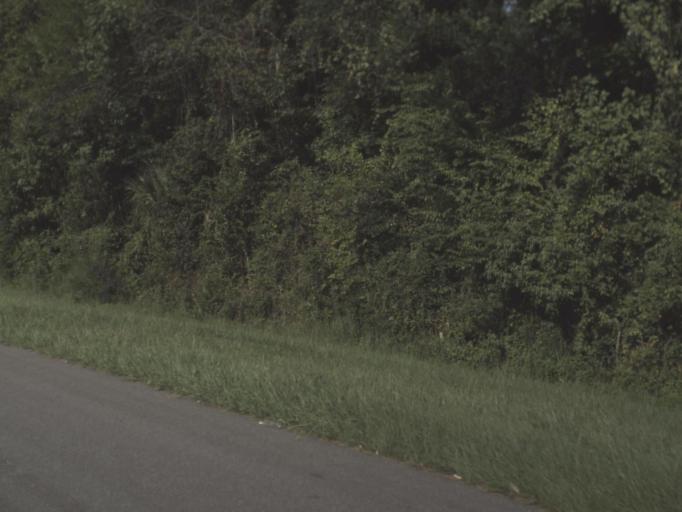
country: US
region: Florida
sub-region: Hillsborough County
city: Lutz
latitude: 28.1435
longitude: -82.4100
